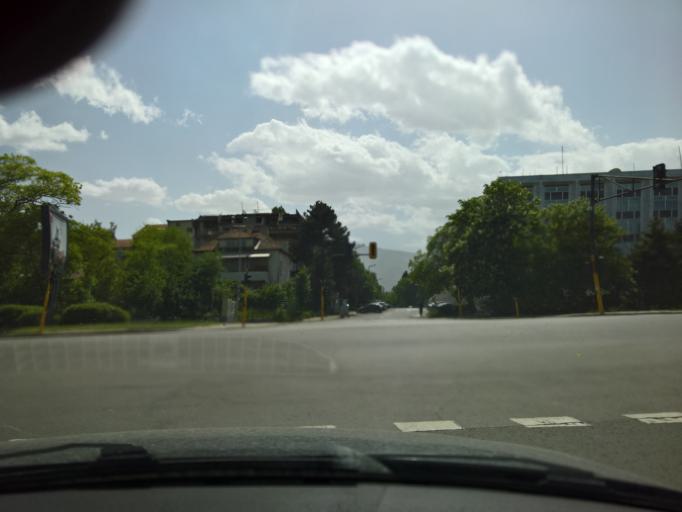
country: BG
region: Sofia-Capital
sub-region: Stolichna Obshtina
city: Sofia
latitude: 42.6725
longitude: 23.3485
